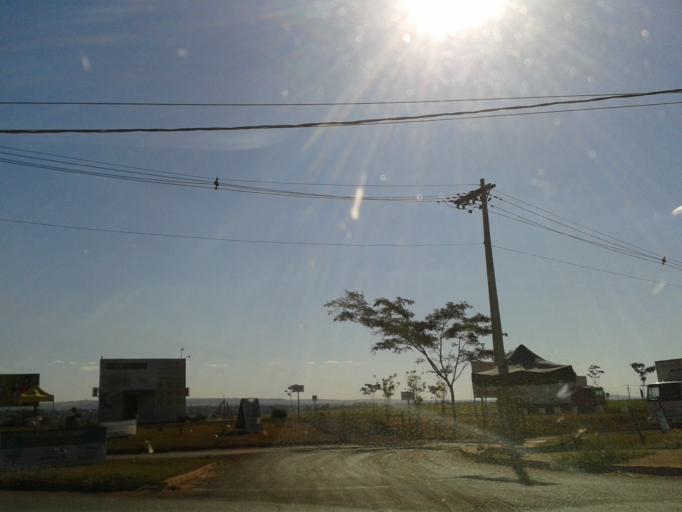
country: BR
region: Goias
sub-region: Itumbiara
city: Itumbiara
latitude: -18.4284
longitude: -49.1947
